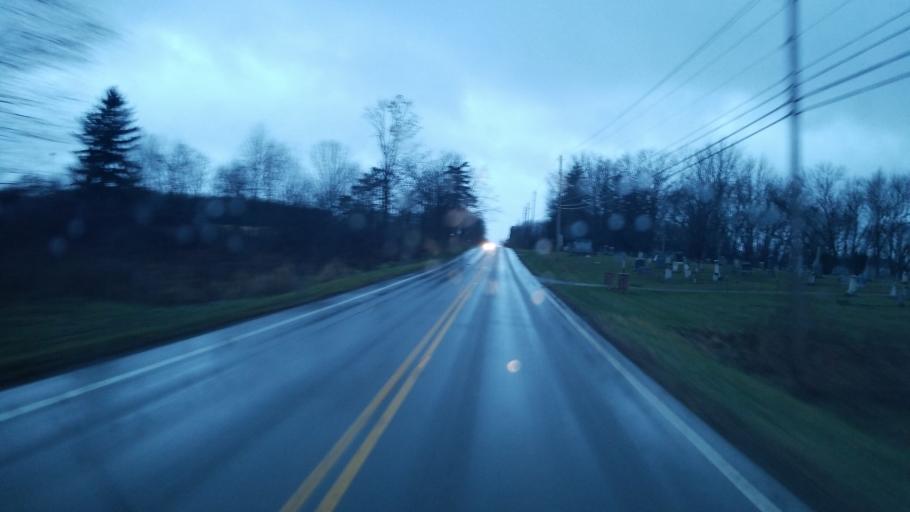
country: US
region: Ohio
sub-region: Ashtabula County
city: Andover
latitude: 41.6070
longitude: -80.6584
